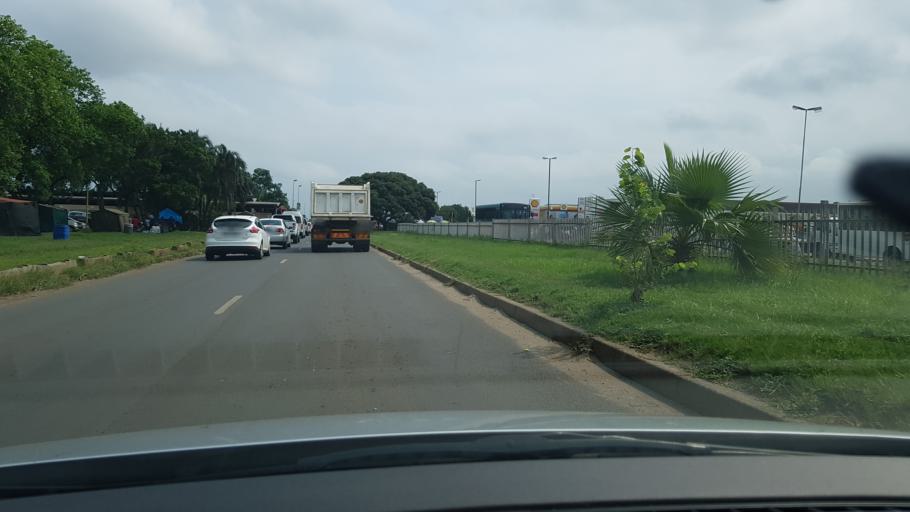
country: ZA
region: KwaZulu-Natal
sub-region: uThungulu District Municipality
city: Richards Bay
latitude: -28.7504
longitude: 32.0484
